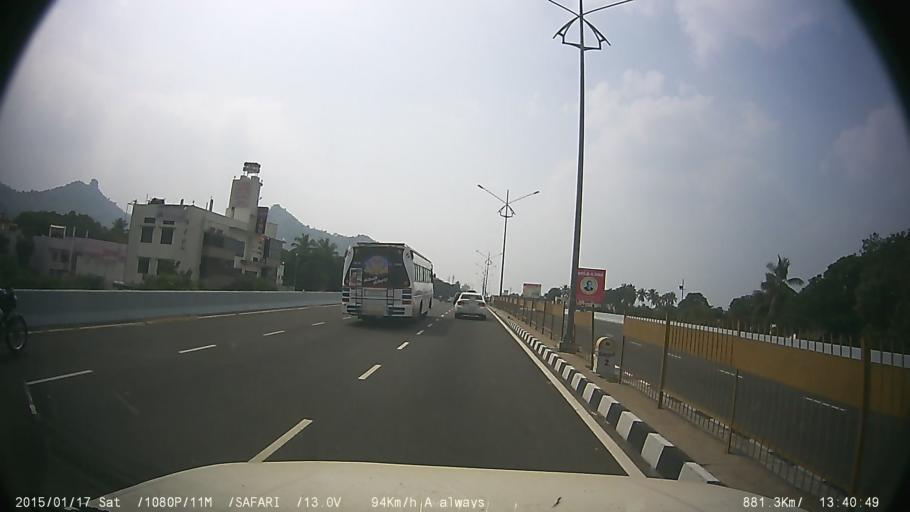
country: IN
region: Tamil Nadu
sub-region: Vellore
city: Vellore
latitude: 12.9373
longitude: 79.1624
